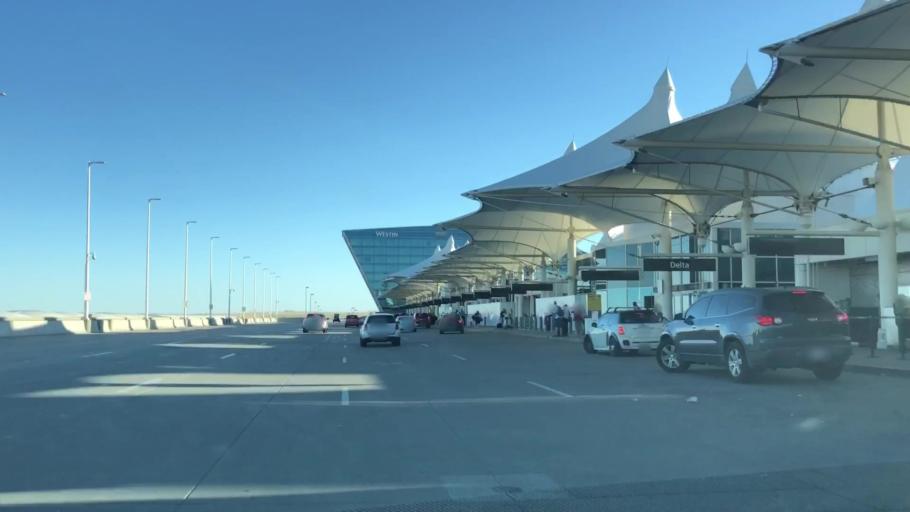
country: US
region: Colorado
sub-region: Weld County
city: Lochbuie
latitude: 39.8503
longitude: -104.6727
